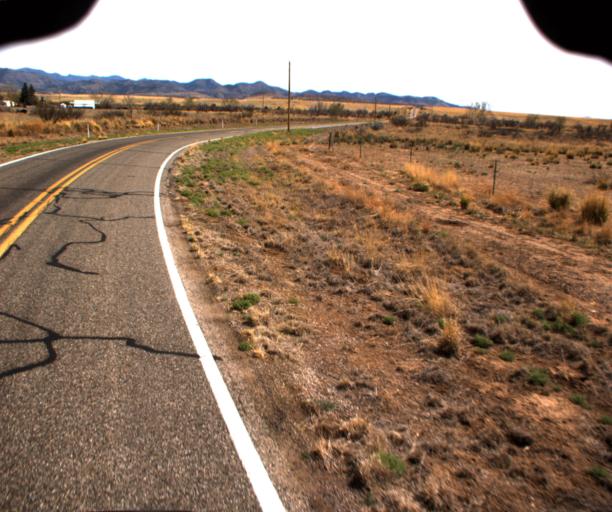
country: US
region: Arizona
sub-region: Cochise County
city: Willcox
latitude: 32.0218
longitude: -109.4404
